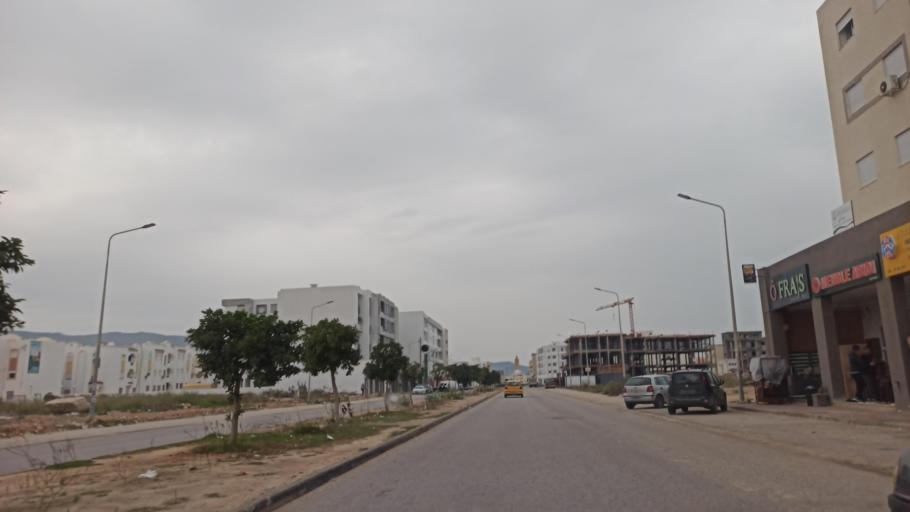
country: TN
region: Tunis
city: Hammam-Lif
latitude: 36.7048
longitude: 10.4167
